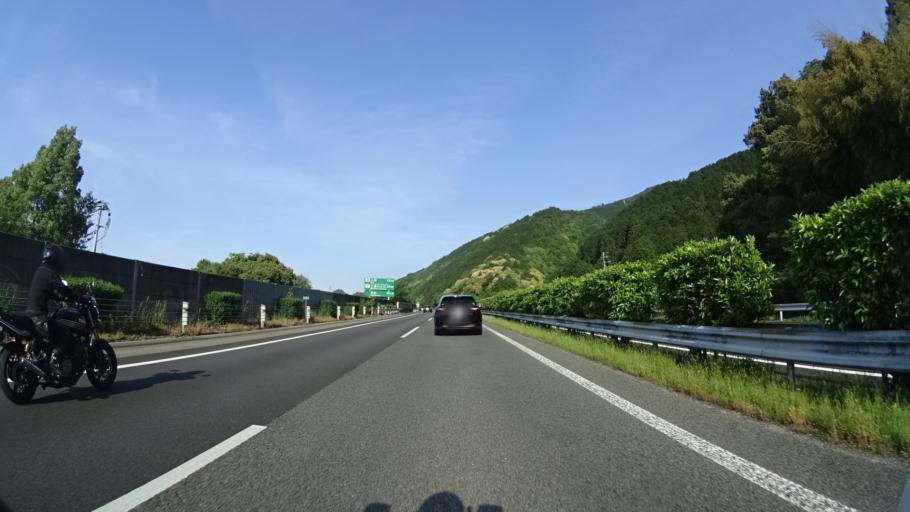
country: JP
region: Ehime
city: Niihama
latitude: 33.9292
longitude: 133.3402
